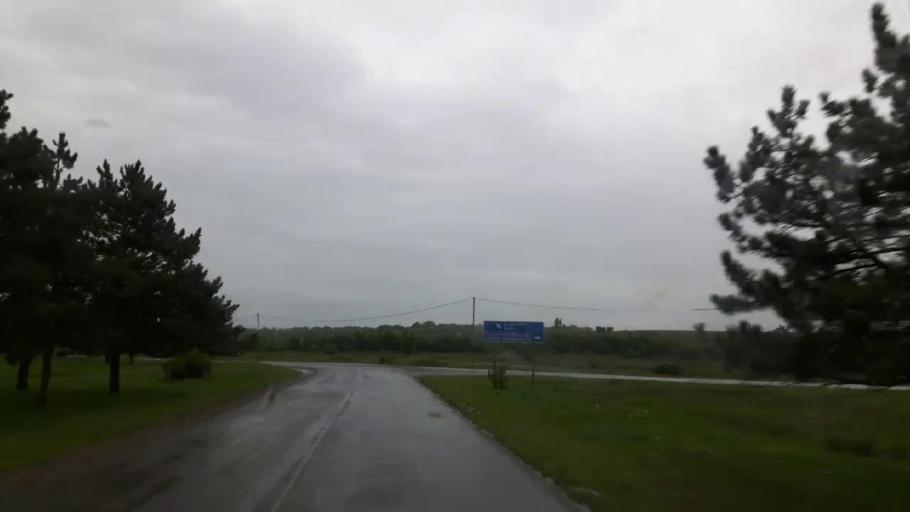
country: GE
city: Agara
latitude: 42.0196
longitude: 43.9053
